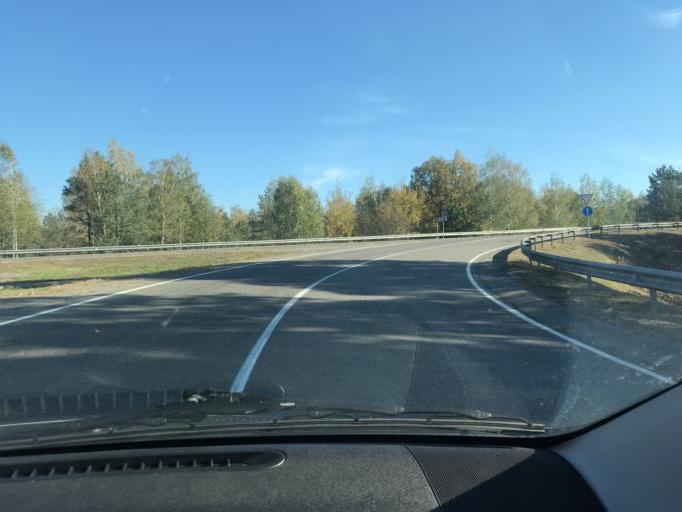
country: BY
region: Brest
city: Mikashevichy
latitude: 52.2458
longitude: 27.4424
